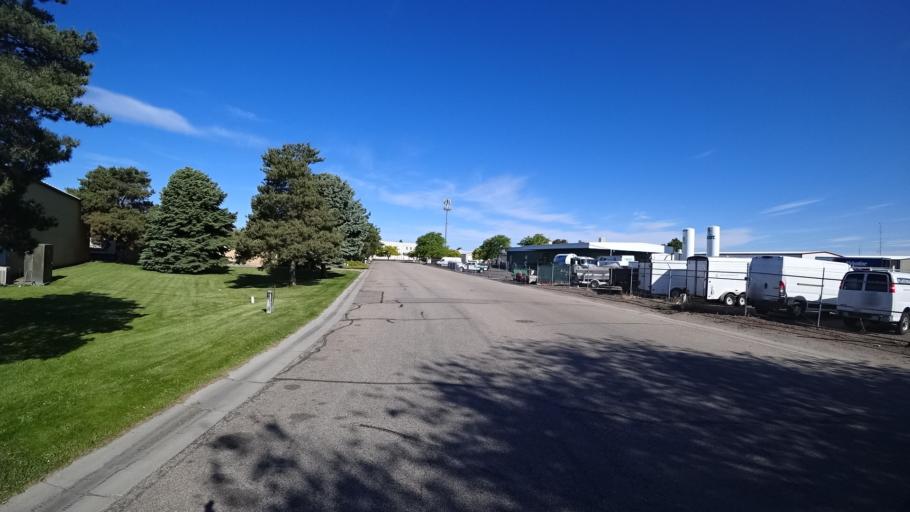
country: US
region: Idaho
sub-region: Ada County
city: Garden City
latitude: 43.5834
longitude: -116.2709
